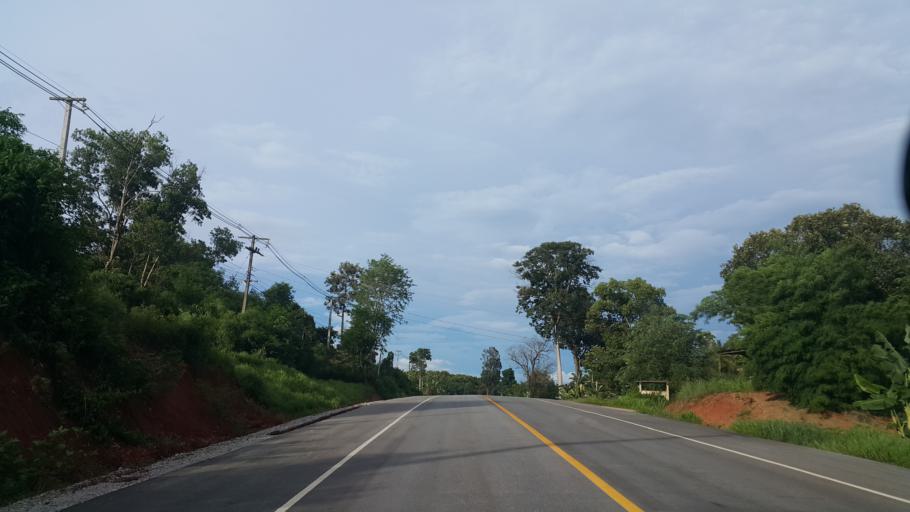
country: TH
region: Loei
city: Na Haeo
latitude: 17.4962
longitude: 101.0302
